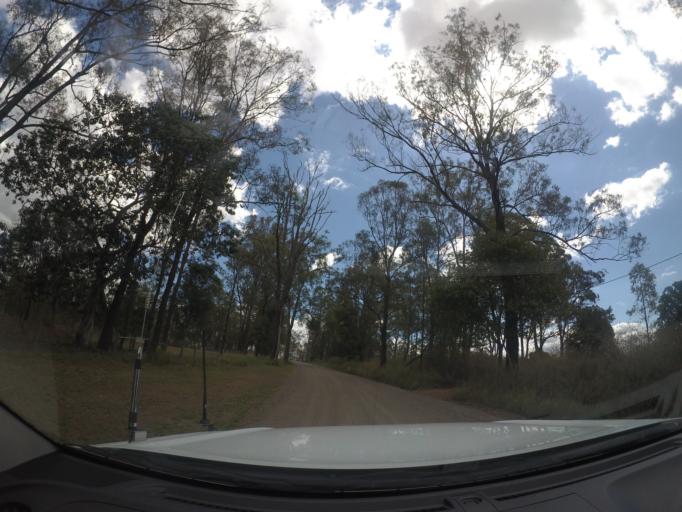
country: AU
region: Queensland
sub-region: Logan
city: Cedar Vale
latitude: -27.8961
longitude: 152.9901
